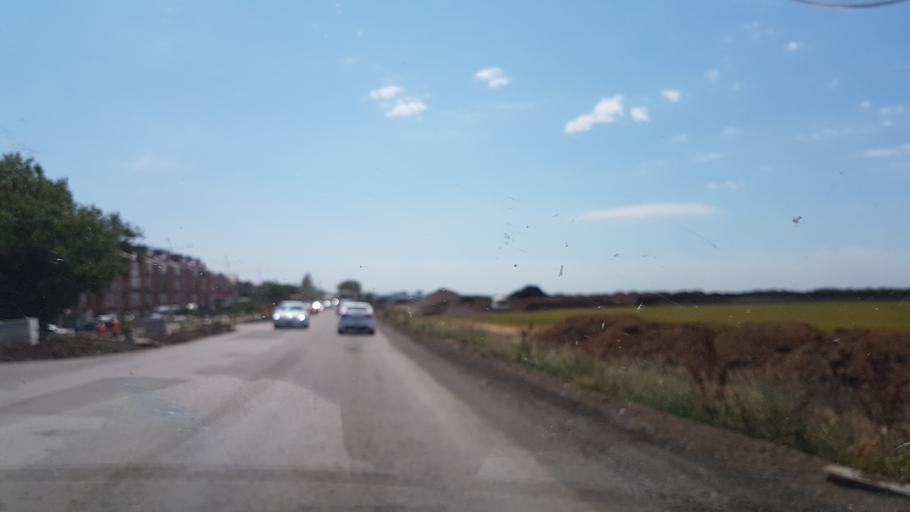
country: RU
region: Rostov
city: Temernik
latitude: 47.3209
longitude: 39.7437
